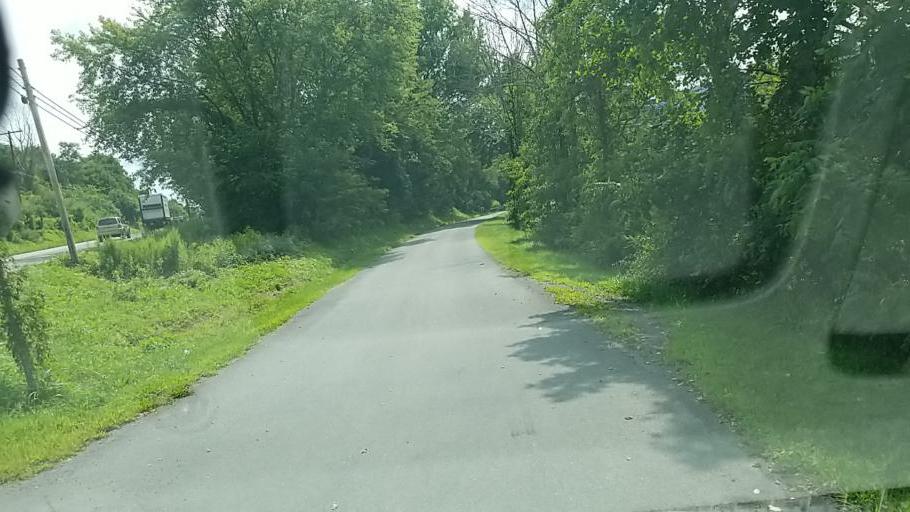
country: US
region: Pennsylvania
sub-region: Dauphin County
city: Elizabethville
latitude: 40.5485
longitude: -76.8737
